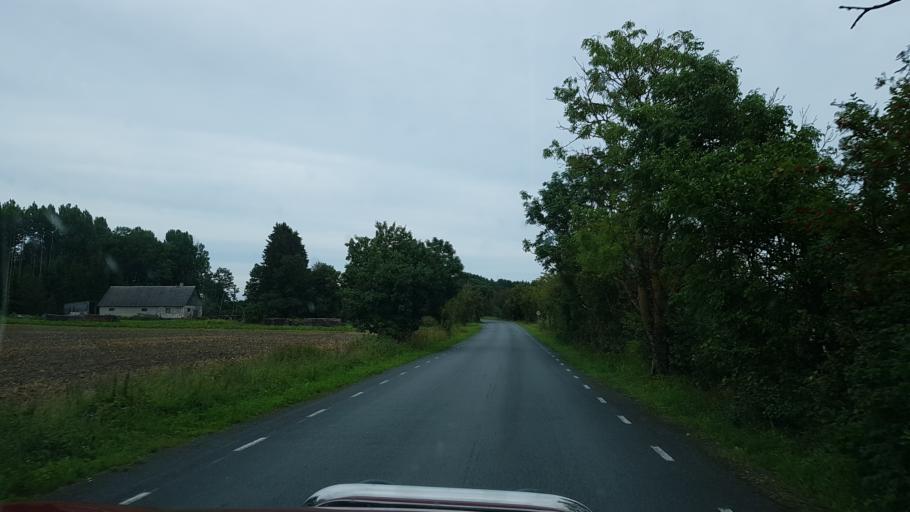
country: EE
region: Laeaene
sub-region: Lihula vald
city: Lihula
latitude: 58.8723
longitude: 23.8989
